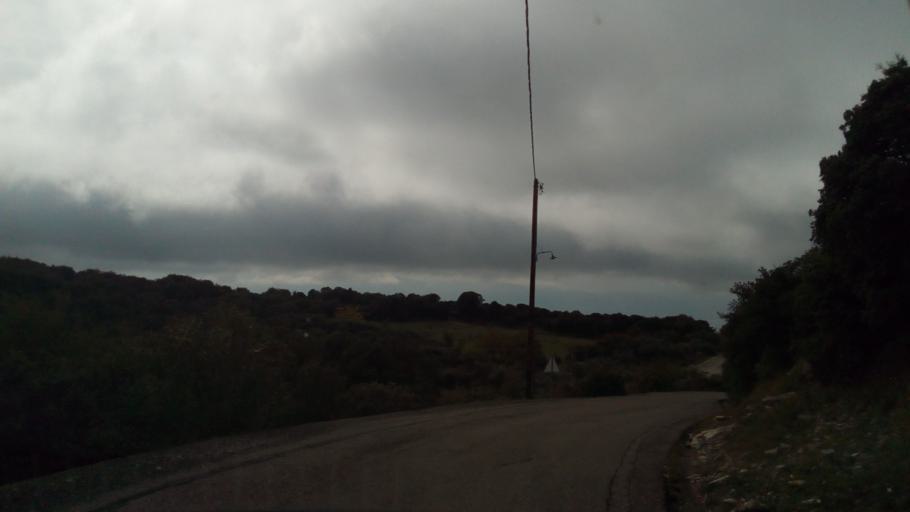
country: GR
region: West Greece
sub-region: Nomos Achaias
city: Kamarai
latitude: 38.4465
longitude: 21.9681
